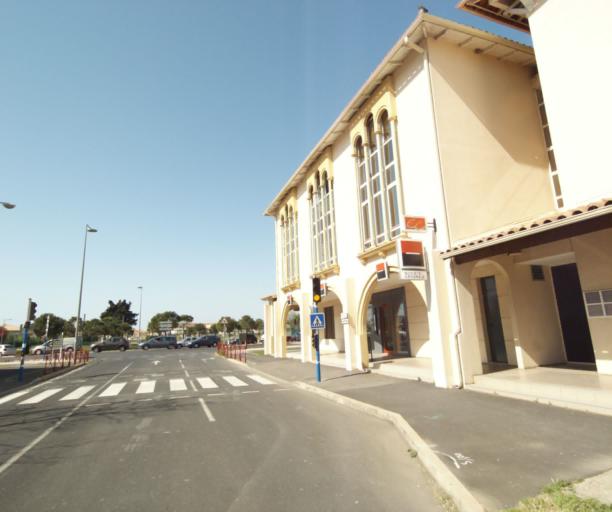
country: FR
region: Languedoc-Roussillon
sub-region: Departement de l'Herault
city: Lattes
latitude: 43.5719
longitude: 3.9068
